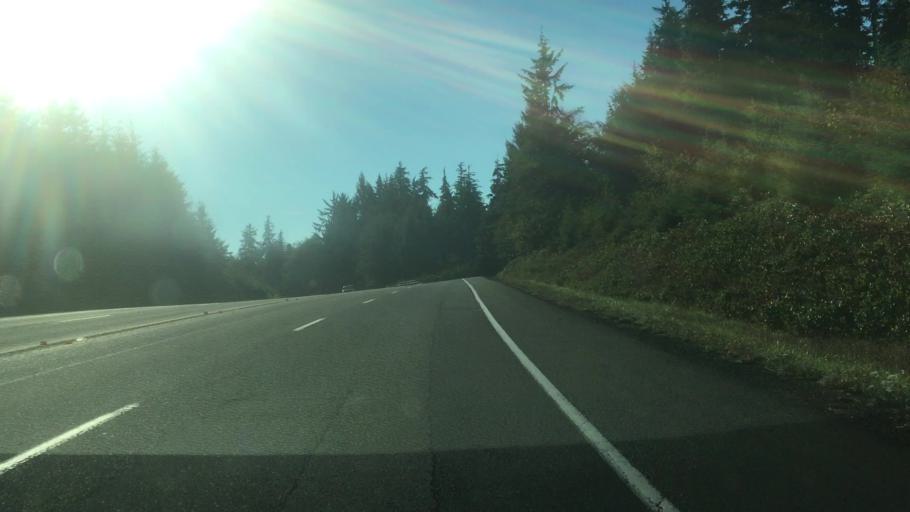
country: US
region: Washington
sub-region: Pacific County
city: South Bend
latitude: 46.6833
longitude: -123.8900
